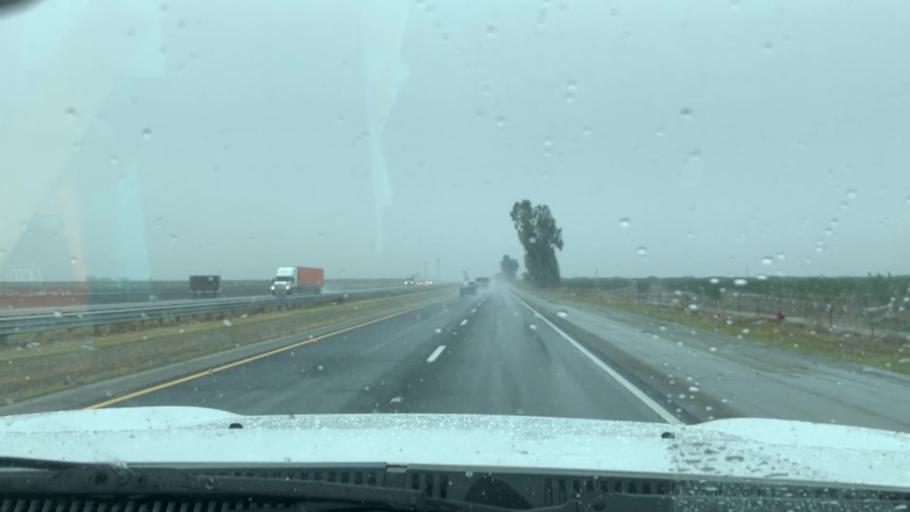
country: US
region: California
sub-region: Tulare County
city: Earlimart
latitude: 35.8507
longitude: -119.2663
